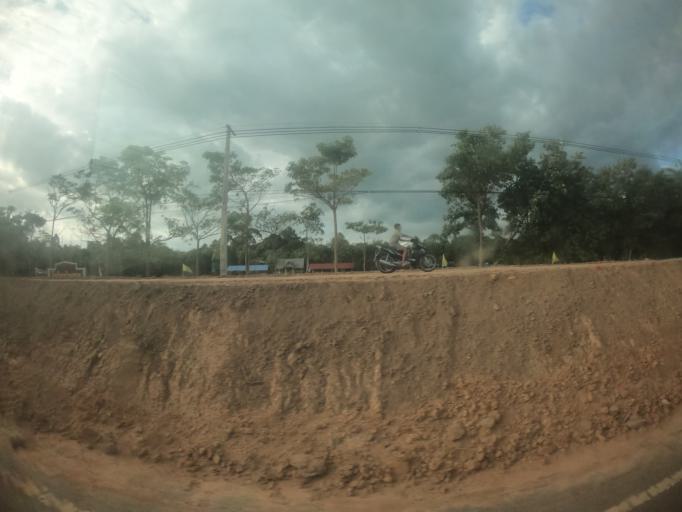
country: TH
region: Surin
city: Kap Choeng
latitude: 14.4657
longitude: 103.6379
